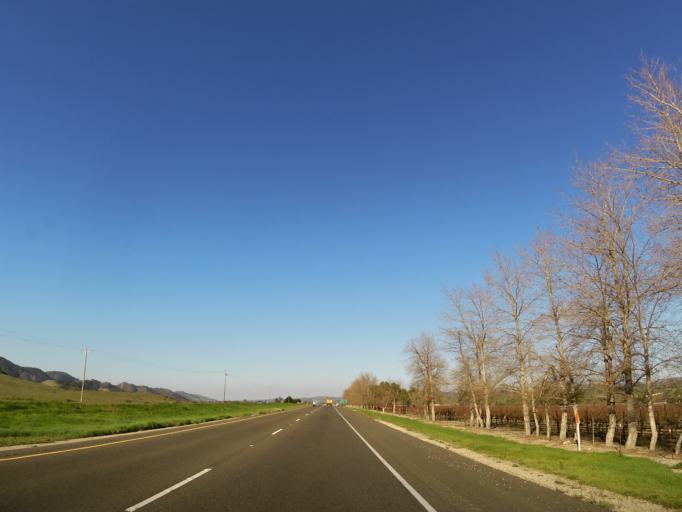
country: US
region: California
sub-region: Santa Barbara County
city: Los Alamos
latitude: 34.7297
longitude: -120.2314
